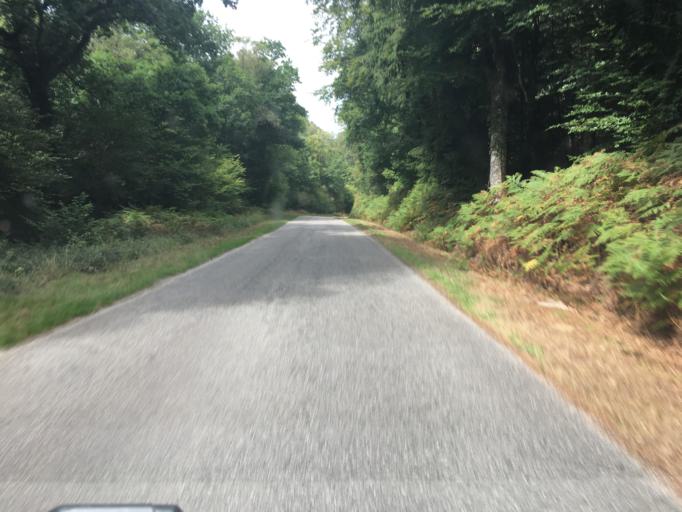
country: FR
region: Brittany
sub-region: Departement des Cotes-d'Armor
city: Gouarec
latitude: 48.2041
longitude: -3.1156
